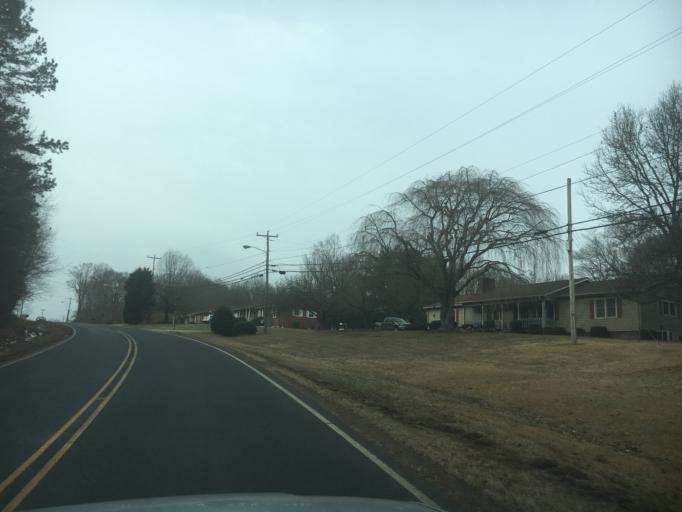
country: US
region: North Carolina
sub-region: Iredell County
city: Statesville
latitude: 35.7961
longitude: -80.8405
